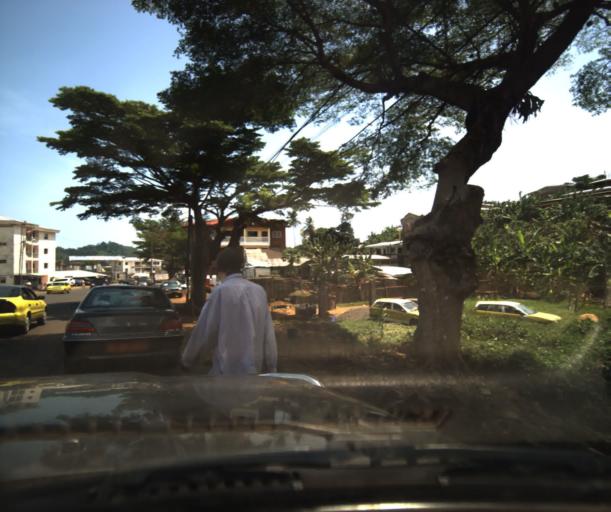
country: CM
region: South-West Province
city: Limbe
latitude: 4.0174
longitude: 9.2083
